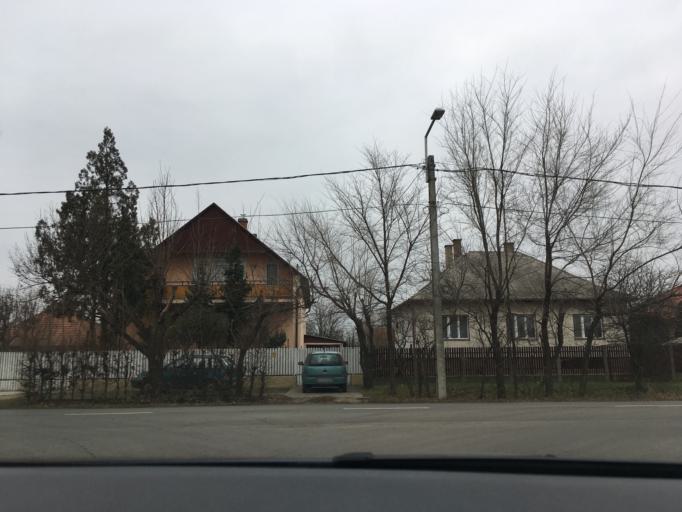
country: HU
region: Hajdu-Bihar
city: Debrecen
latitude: 47.5501
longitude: 21.6715
